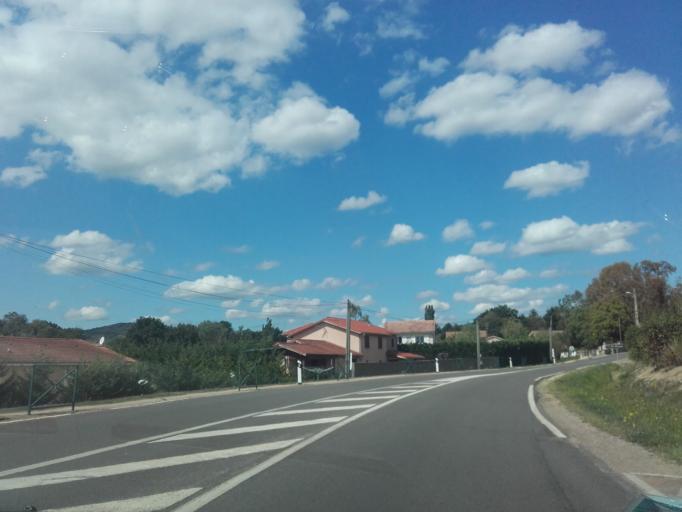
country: FR
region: Bourgogne
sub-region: Departement de Saone-et-Loire
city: La Chapelle-de-Guinchay
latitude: 46.2141
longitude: 4.7572
